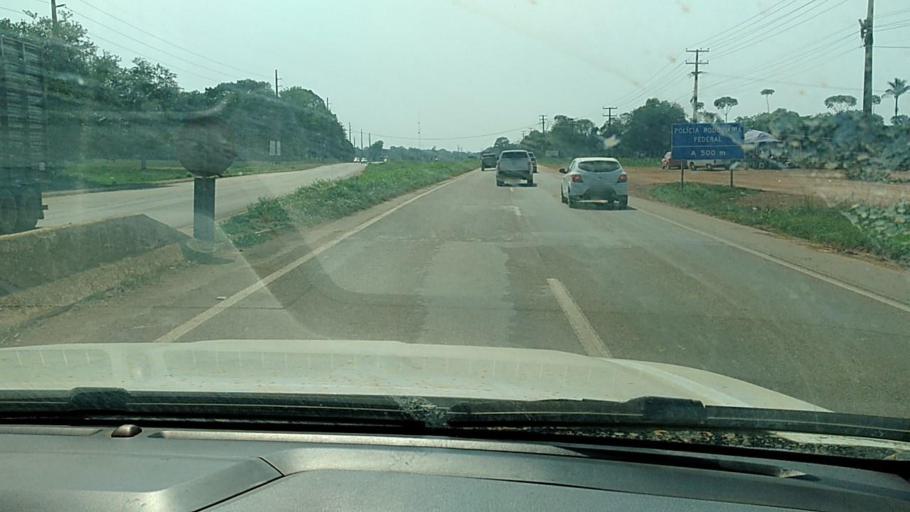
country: BR
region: Rondonia
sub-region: Porto Velho
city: Porto Velho
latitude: -8.8006
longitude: -63.7678
